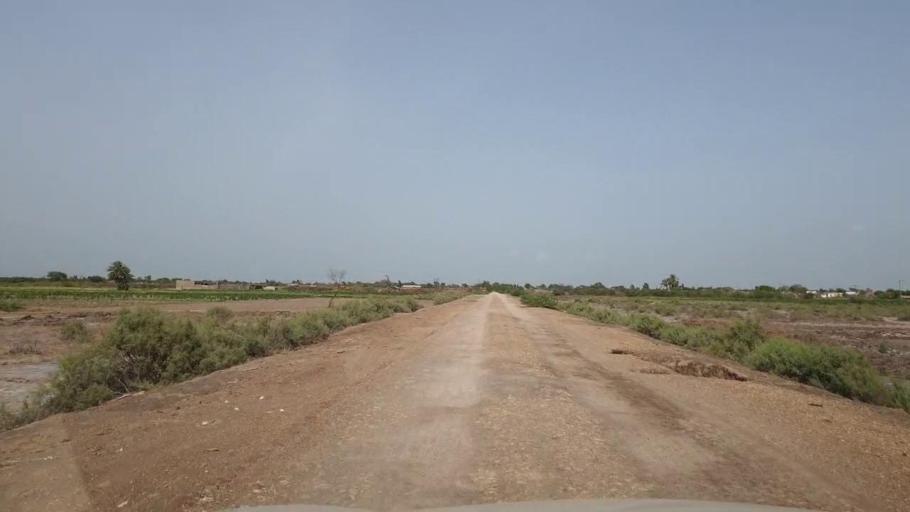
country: PK
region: Sindh
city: Mirwah Gorchani
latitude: 25.2778
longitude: 68.9516
